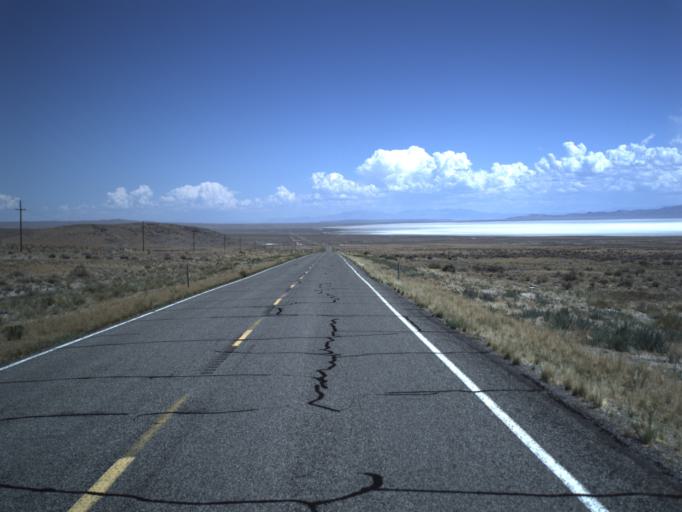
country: US
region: Utah
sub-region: Beaver County
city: Milford
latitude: 39.0493
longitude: -113.2759
